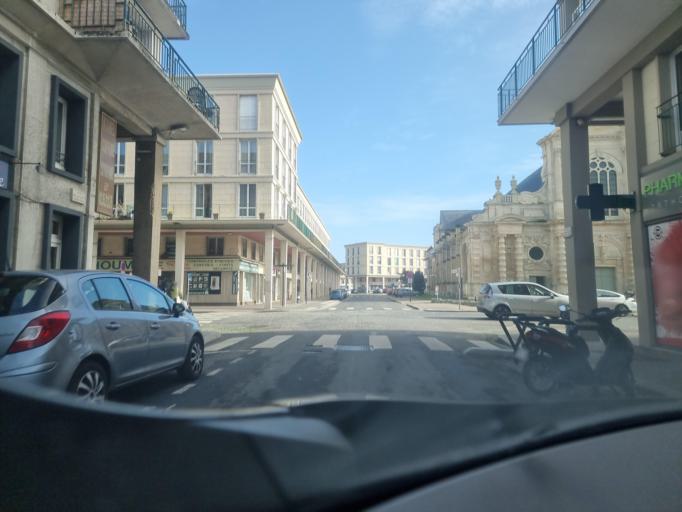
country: FR
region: Haute-Normandie
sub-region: Departement de la Seine-Maritime
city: Le Havre
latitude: 49.4873
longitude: 0.1070
